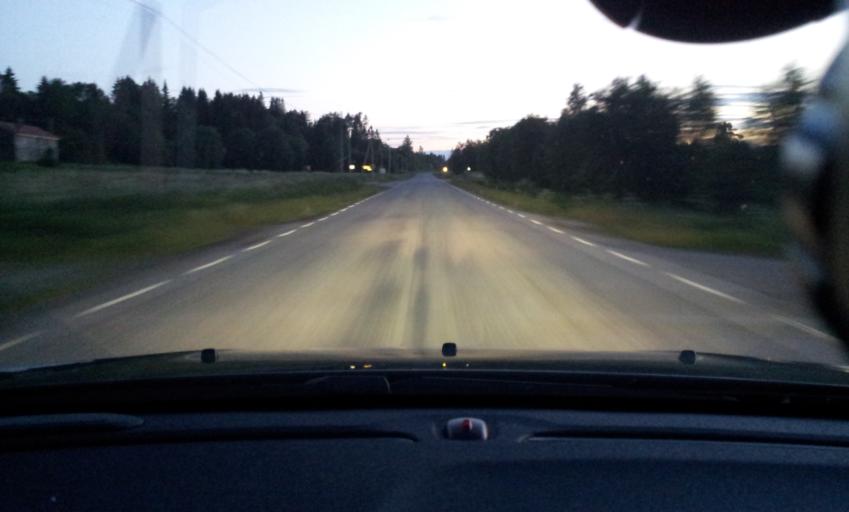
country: SE
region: Jaemtland
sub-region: Bergs Kommun
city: Hoverberg
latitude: 62.7842
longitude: 14.5026
